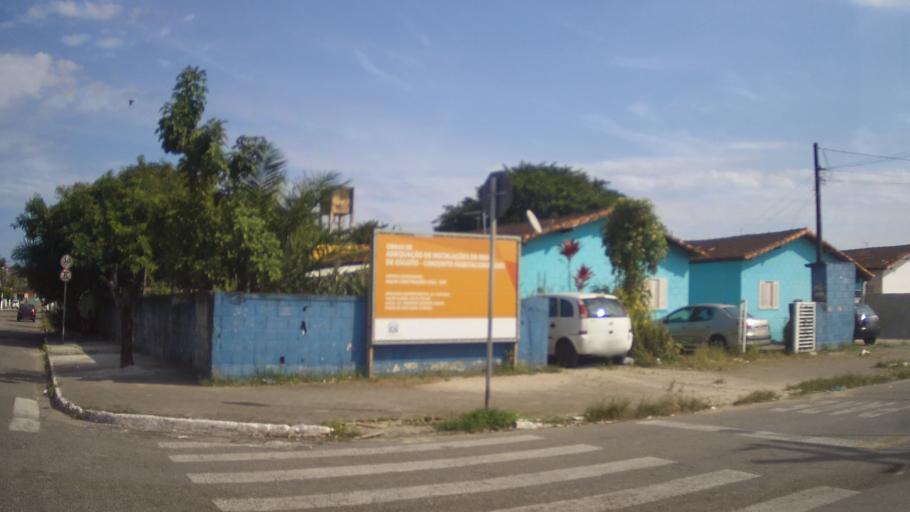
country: BR
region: Sao Paulo
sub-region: Praia Grande
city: Praia Grande
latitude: -23.9994
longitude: -46.4298
